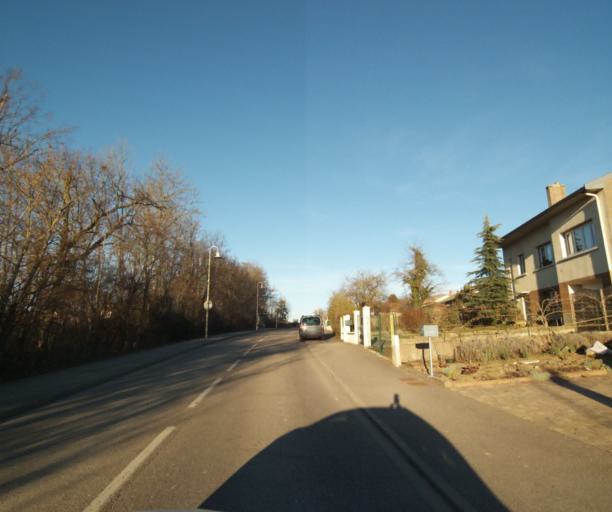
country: FR
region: Lorraine
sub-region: Departement de Meurthe-et-Moselle
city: Art-sur-Meurthe
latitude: 48.6582
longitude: 6.2687
